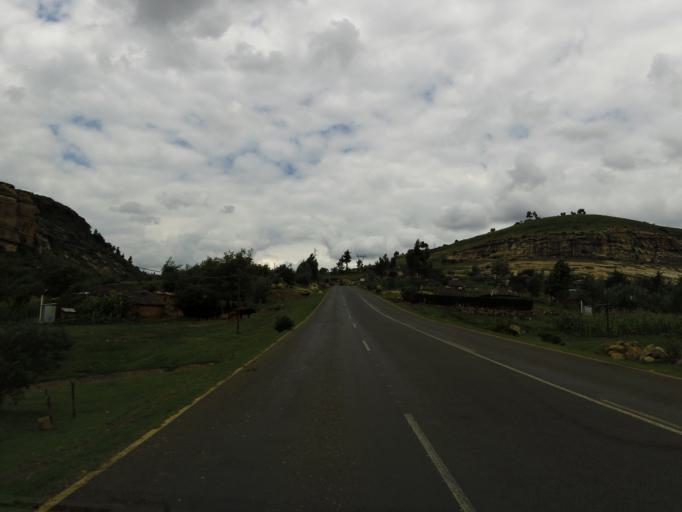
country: LS
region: Leribe
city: Leribe
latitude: -28.9883
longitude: 28.1847
